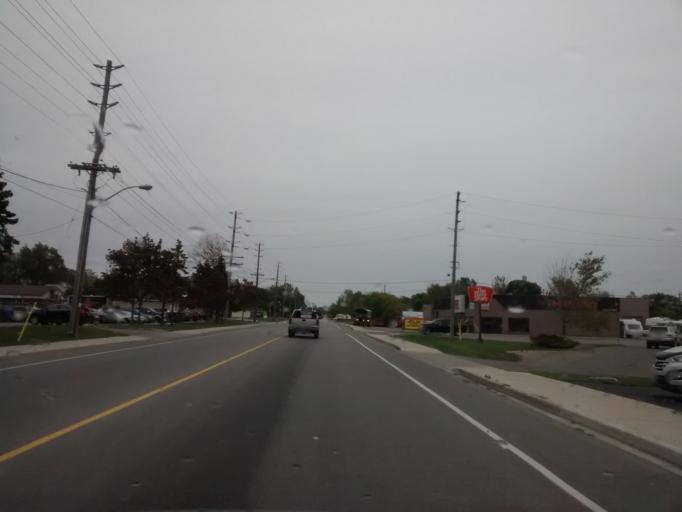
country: CA
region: Ontario
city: Welland
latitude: 42.9016
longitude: -79.6161
